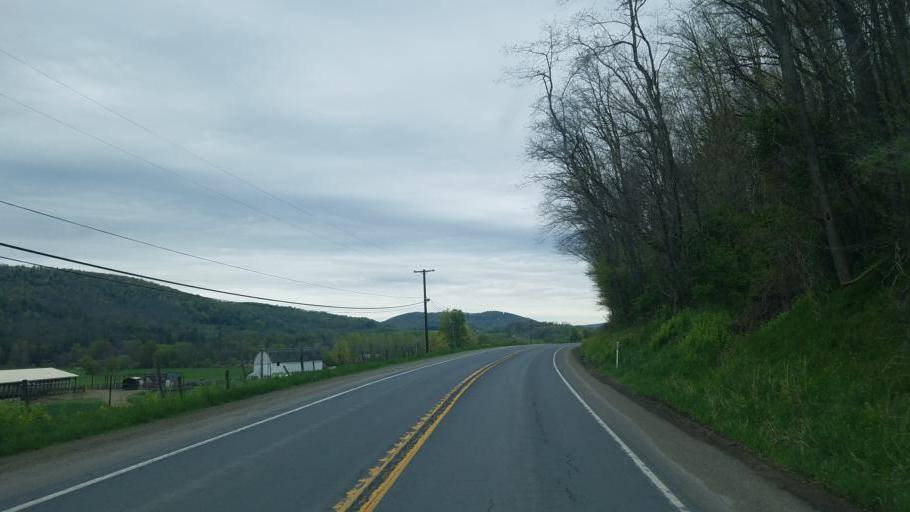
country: US
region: Pennsylvania
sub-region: Tioga County
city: Westfield
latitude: 41.9568
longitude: -77.4462
